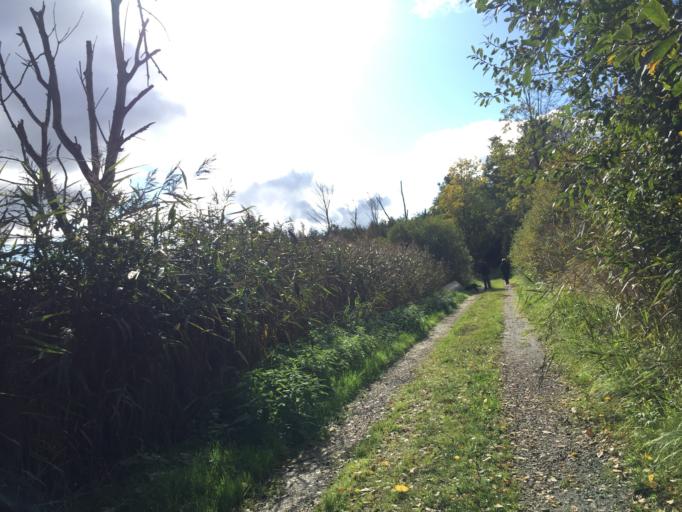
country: DK
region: Zealand
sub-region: Koge Kommune
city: Borup
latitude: 55.4711
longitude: 11.8959
